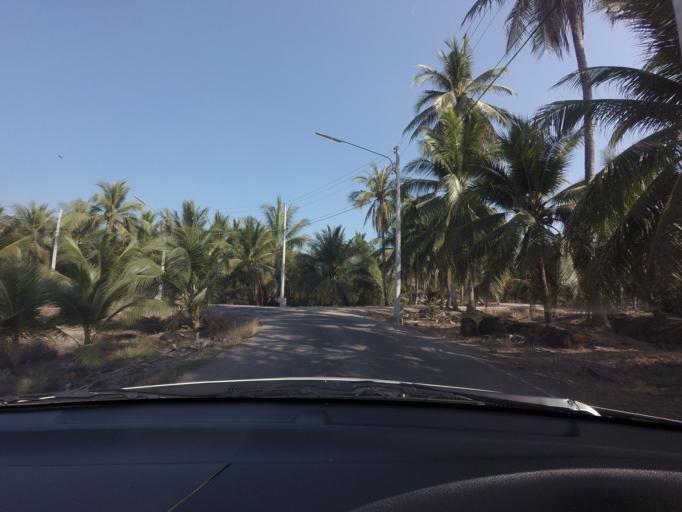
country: TH
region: Ratchaburi
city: Damnoen Saduak
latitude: 13.4860
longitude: 100.0007
